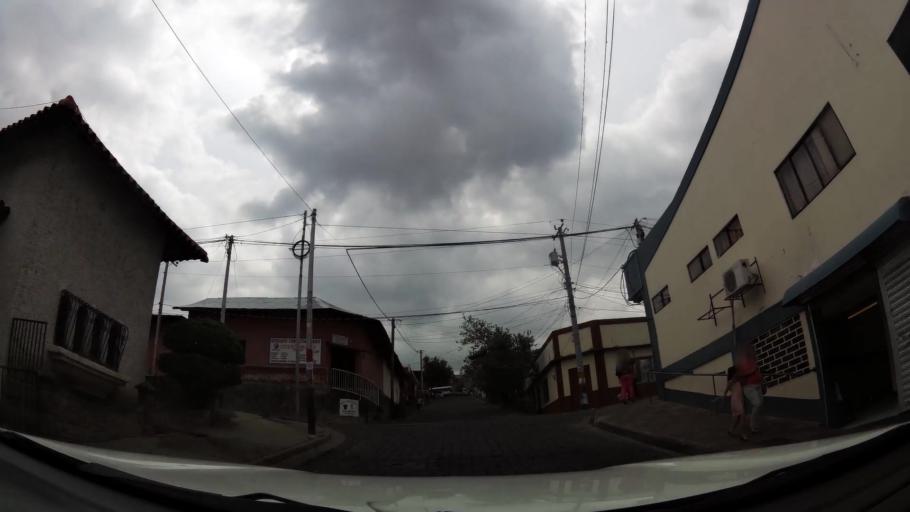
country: NI
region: Matagalpa
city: Matagalpa
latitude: 12.9226
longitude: -85.9177
